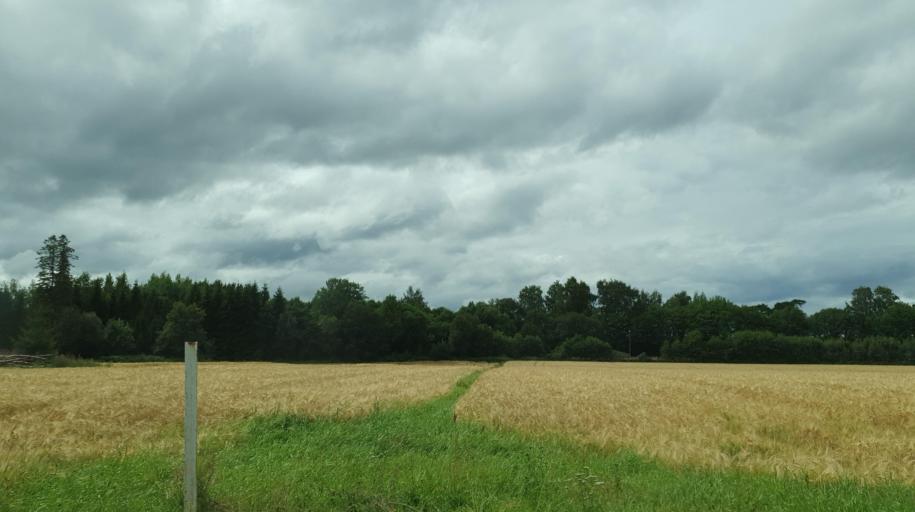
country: NO
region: Nord-Trondelag
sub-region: Stjordal
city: Stjordalshalsen
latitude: 63.4602
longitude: 10.9476
